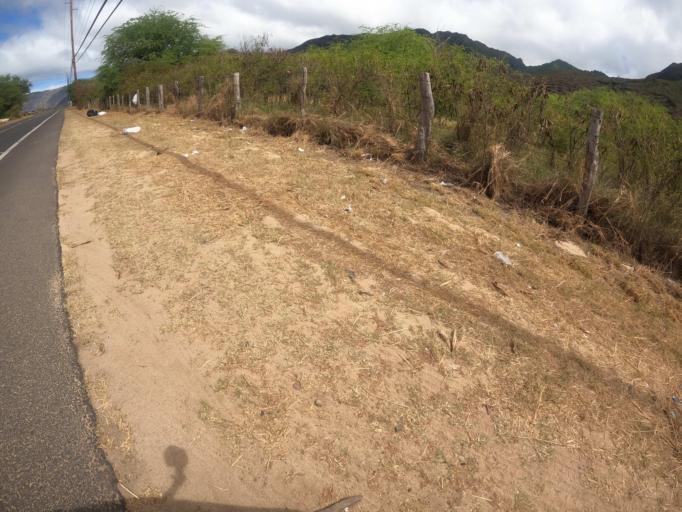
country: US
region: Hawaii
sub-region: Honolulu County
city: Makaha
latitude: 21.4984
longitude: -158.2293
